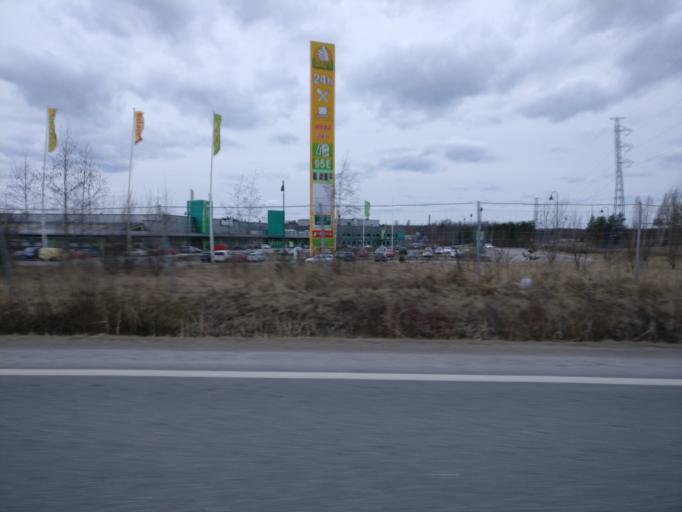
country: FI
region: Uusimaa
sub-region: Helsinki
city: Hyvinge
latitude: 60.6192
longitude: 24.8082
